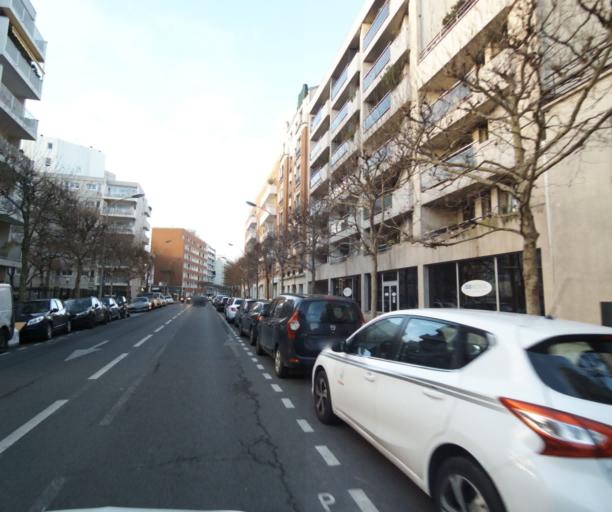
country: FR
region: Ile-de-France
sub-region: Departement des Hauts-de-Seine
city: Courbevoie
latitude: 48.9023
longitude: 2.2653
